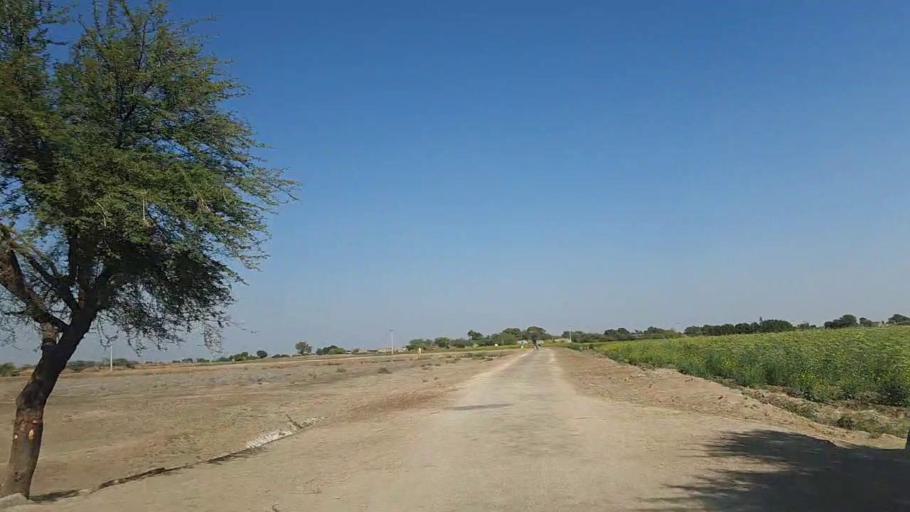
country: PK
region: Sindh
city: Naukot
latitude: 25.0064
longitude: 69.3395
